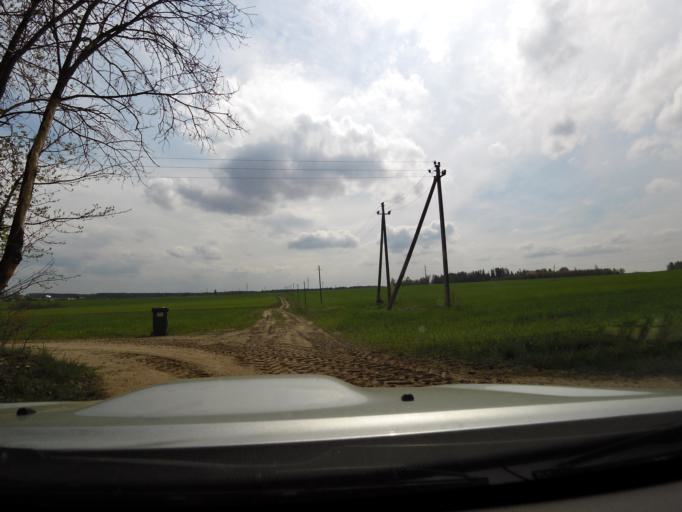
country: LT
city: Salcininkai
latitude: 54.4225
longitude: 25.3088
